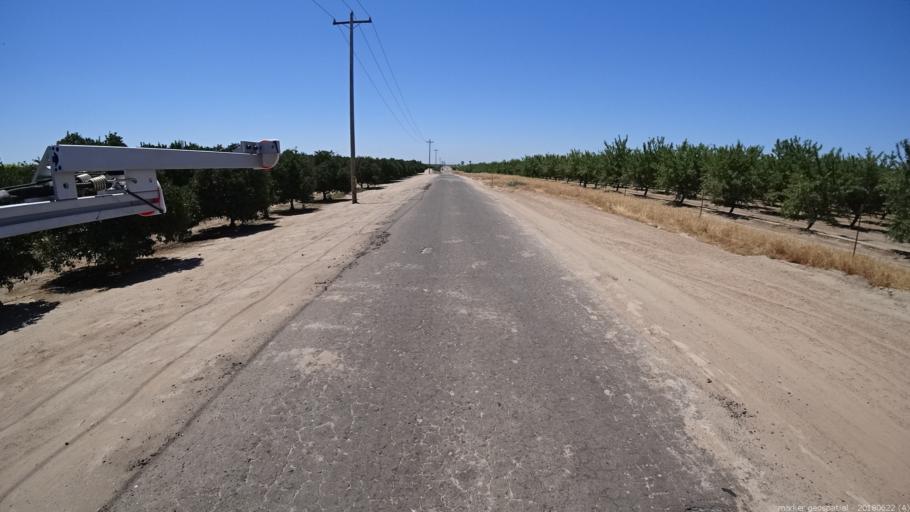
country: US
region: California
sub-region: Madera County
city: Bonadelle Ranchos-Madera Ranchos
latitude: 36.9368
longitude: -119.8306
